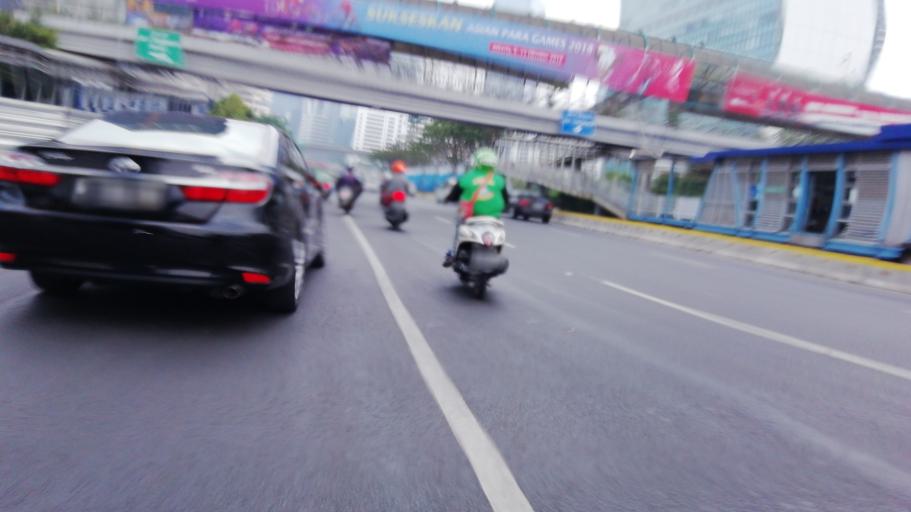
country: ID
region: Jakarta Raya
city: Jakarta
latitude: -6.2170
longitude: 106.8149
